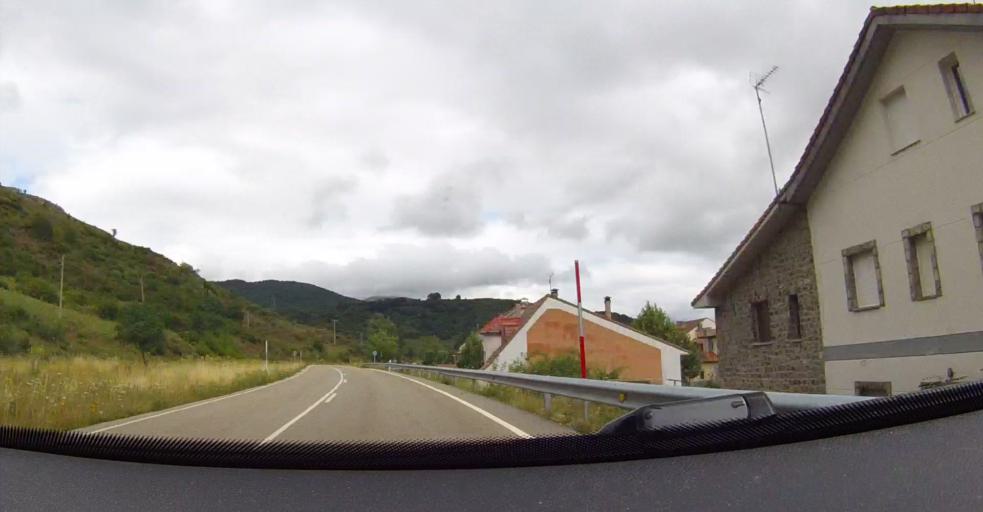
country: ES
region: Castille and Leon
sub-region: Provincia de Leon
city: Buron
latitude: 43.0254
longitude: -5.0535
